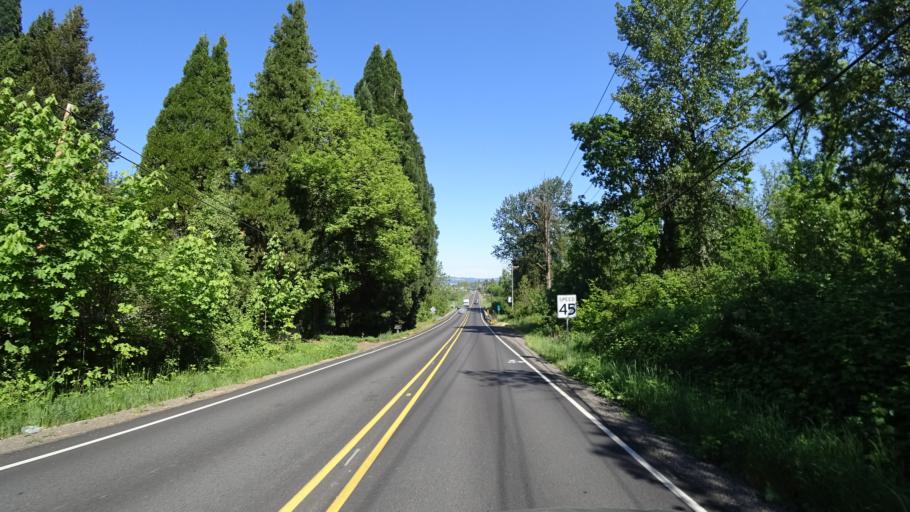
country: US
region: Oregon
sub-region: Washington County
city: Rockcreek
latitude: 45.5595
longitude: -122.8777
